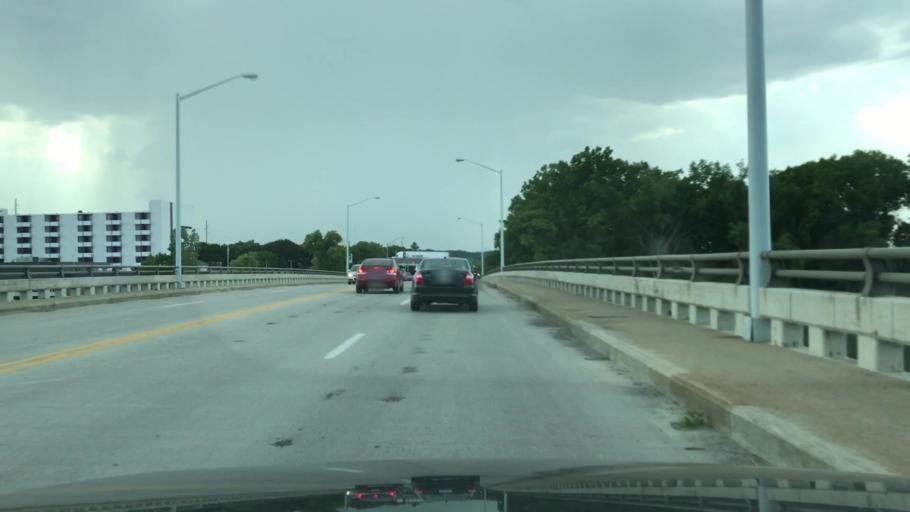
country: US
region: Michigan
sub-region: Kent County
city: Grand Rapids
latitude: 42.9956
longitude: -85.6725
